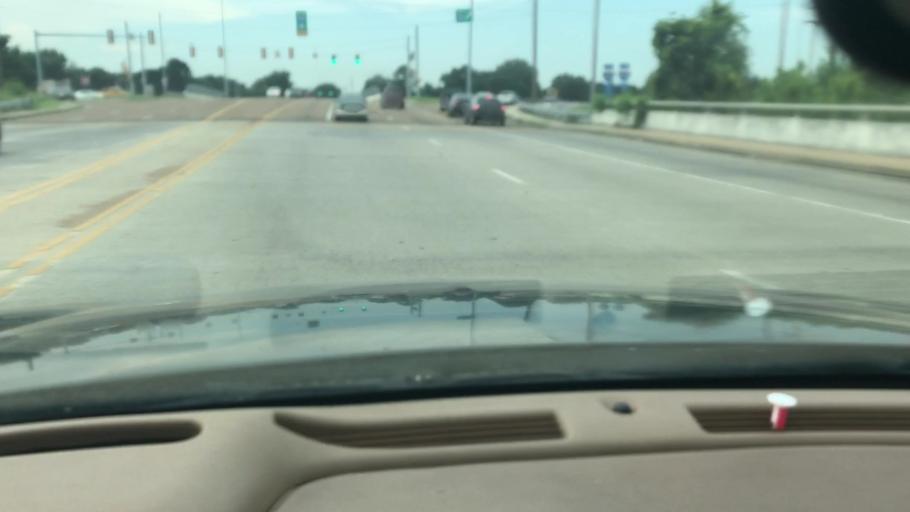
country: US
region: Tennessee
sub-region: Shelby County
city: Germantown
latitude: 35.0767
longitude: -89.9065
